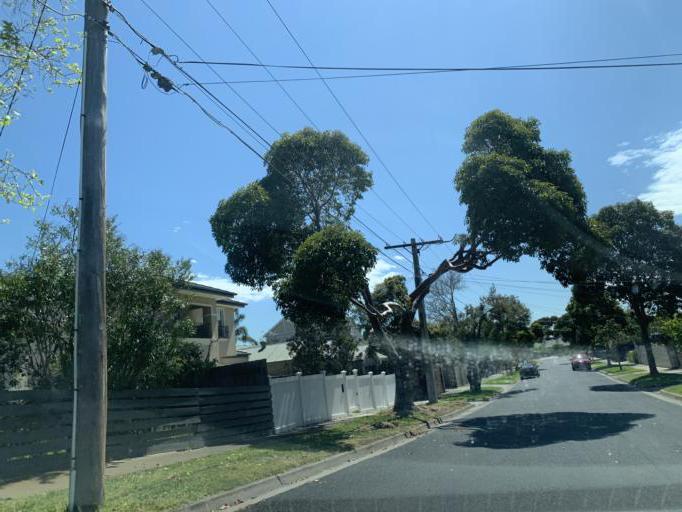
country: AU
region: Victoria
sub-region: Bayside
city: Highett
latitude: -37.9456
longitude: 145.0346
